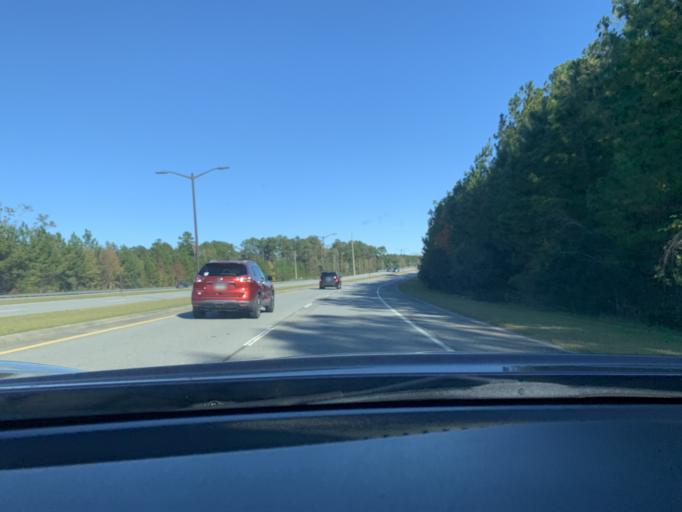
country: US
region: Georgia
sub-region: Chatham County
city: Pooler
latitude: 32.1176
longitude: -81.2691
